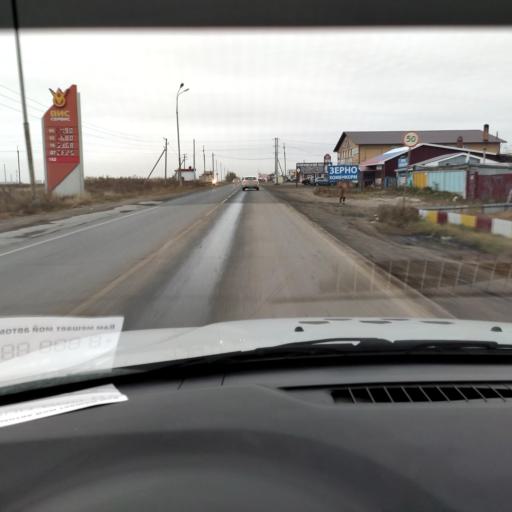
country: RU
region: Samara
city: Podstepki
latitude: 53.5168
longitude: 49.2180
